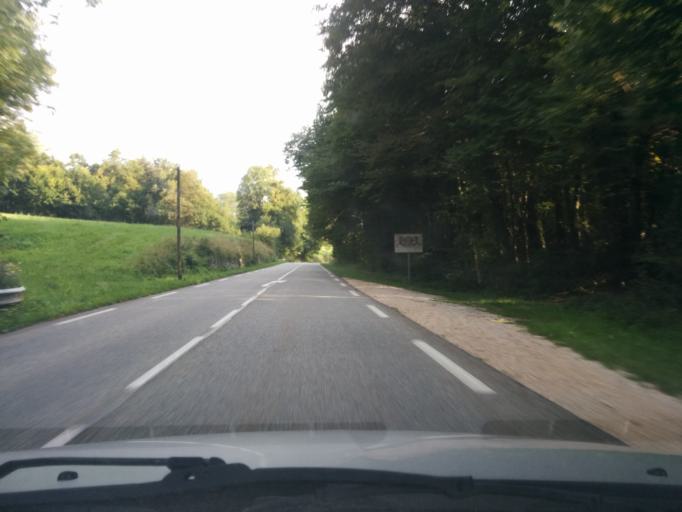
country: FR
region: Rhone-Alpes
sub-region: Departement de la Savoie
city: Les Echelles
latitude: 45.4615
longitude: 5.7372
